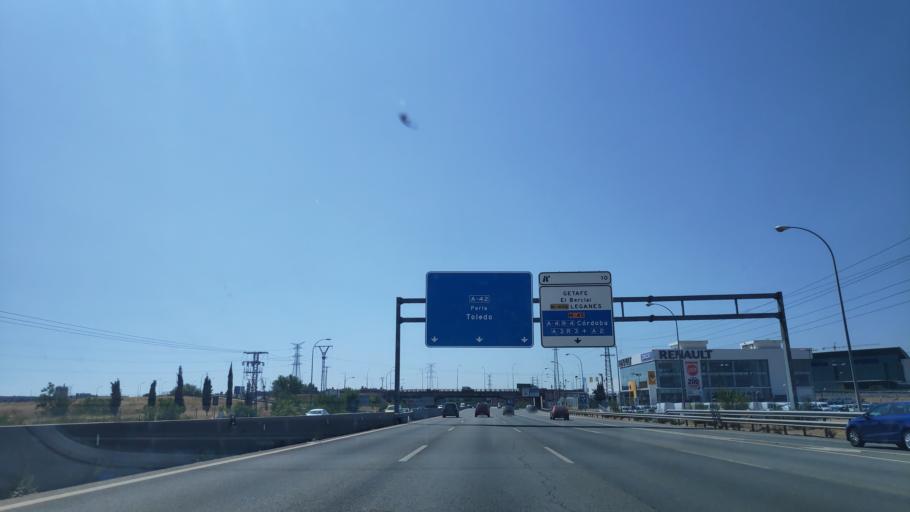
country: ES
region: Madrid
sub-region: Provincia de Madrid
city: Villaverde
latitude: 40.3342
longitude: -3.7249
